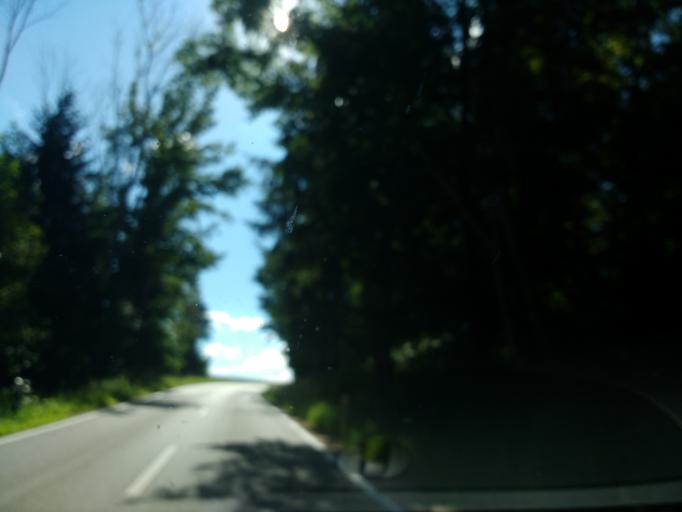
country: DE
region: Bavaria
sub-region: Upper Bavaria
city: Engelsberg
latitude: 48.1238
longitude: 12.5090
